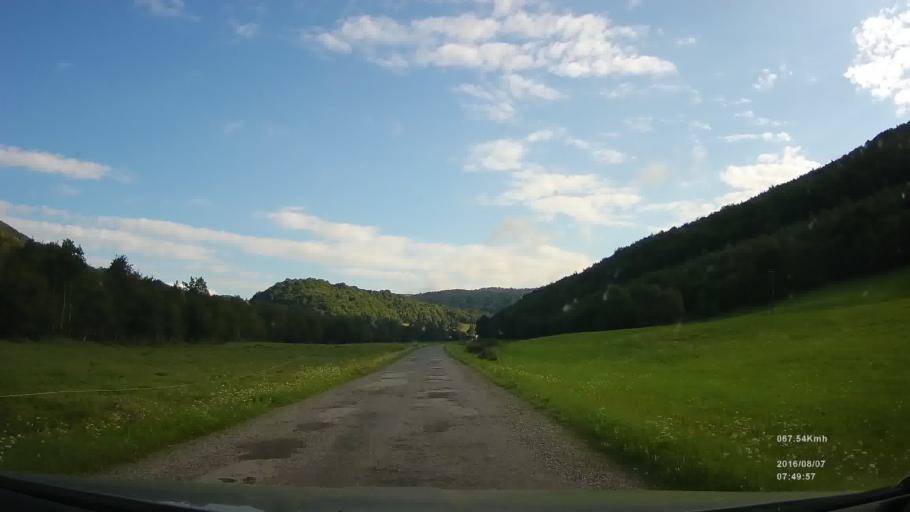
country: SK
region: Presovsky
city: Medzilaborce
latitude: 49.2940
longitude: 21.7755
